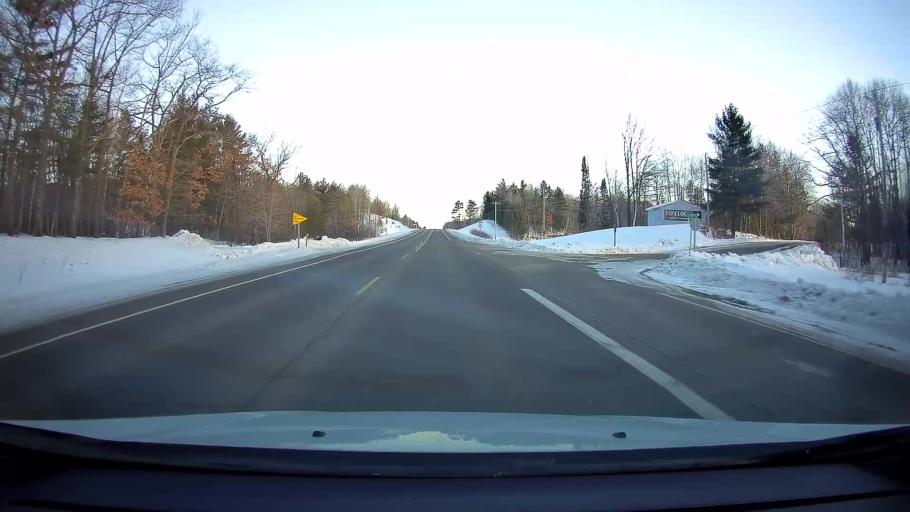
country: US
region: Wisconsin
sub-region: Barron County
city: Cumberland
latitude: 45.5817
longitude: -92.0176
